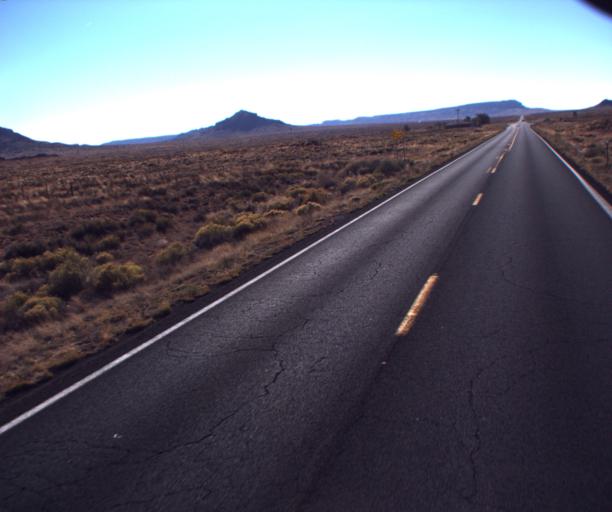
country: US
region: Arizona
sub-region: Navajo County
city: Dilkon
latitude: 35.4984
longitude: -110.4338
